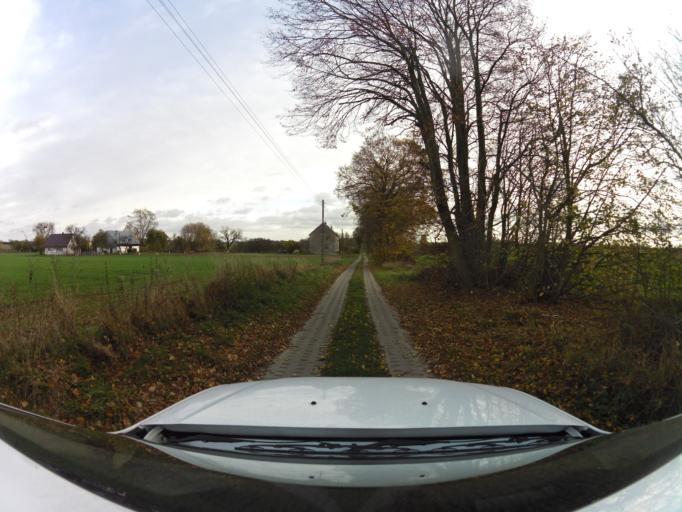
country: PL
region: West Pomeranian Voivodeship
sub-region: Powiat gryficki
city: Gryfice
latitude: 53.8304
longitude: 15.1198
